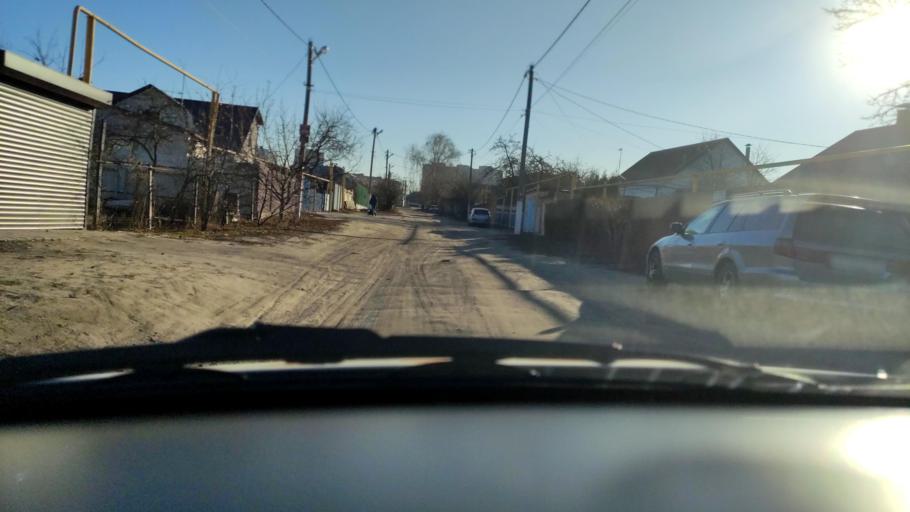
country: RU
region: Voronezj
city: Podgornoye
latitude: 51.7301
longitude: 39.1557
